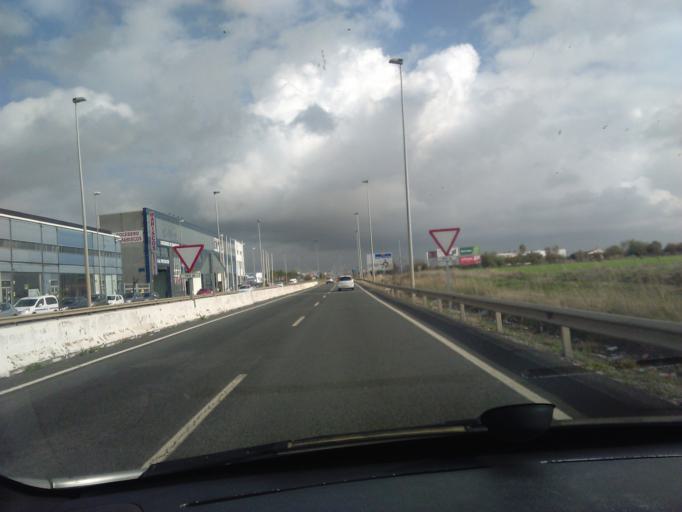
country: ES
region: Andalusia
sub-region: Provincia de Sevilla
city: Sevilla
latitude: 37.3744
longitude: -5.9167
